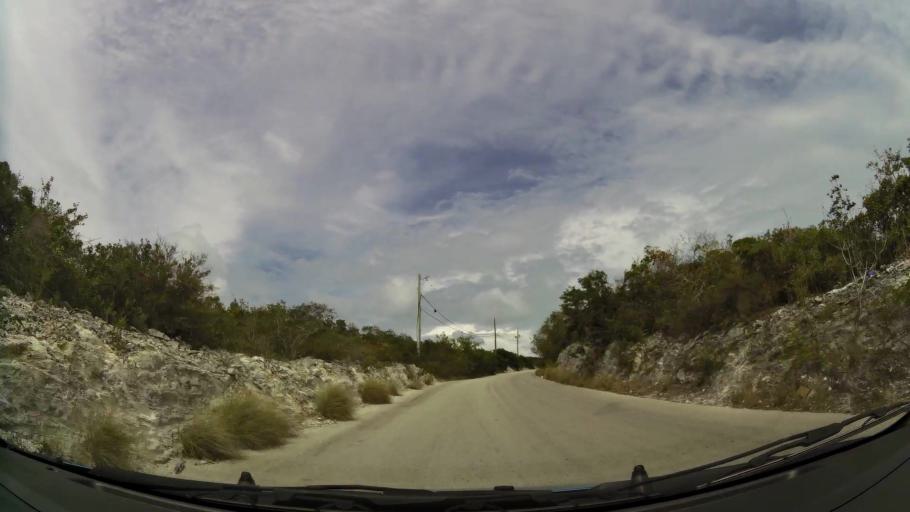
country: BS
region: Mayaguana
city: Abraham's Bay
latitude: 21.7820
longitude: -72.2389
